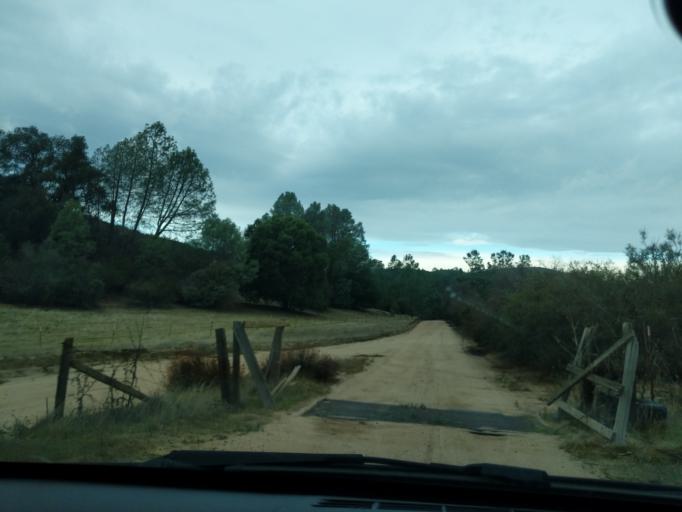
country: US
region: California
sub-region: Monterey County
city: Soledad
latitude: 36.5530
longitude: -121.2663
